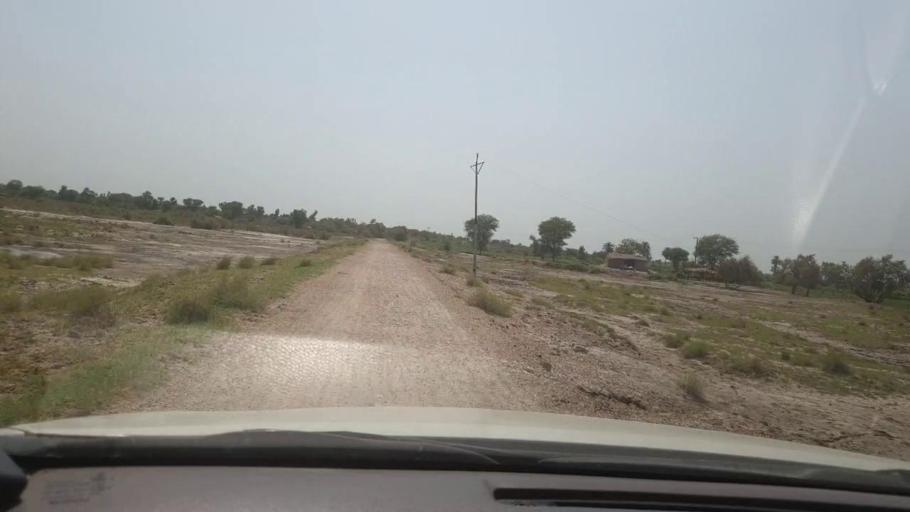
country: PK
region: Sindh
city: Shikarpur
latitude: 27.9208
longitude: 68.6045
